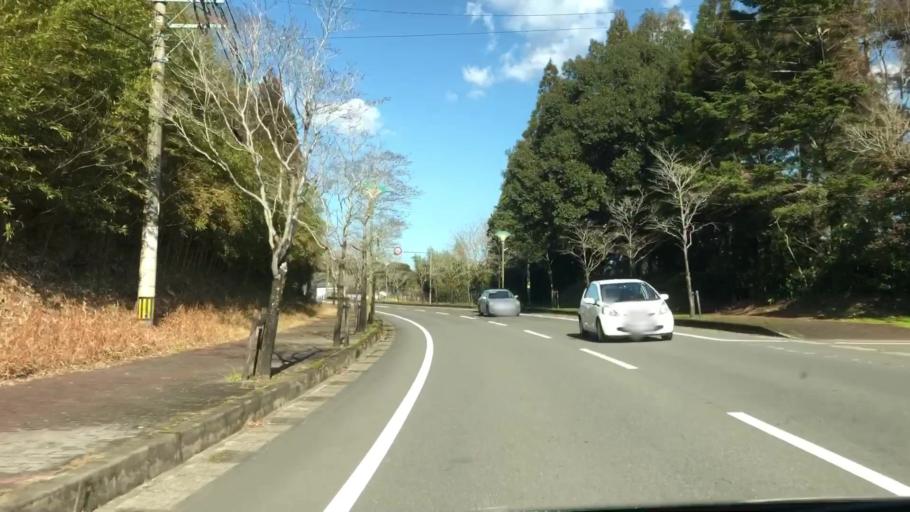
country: JP
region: Kagoshima
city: Satsumasendai
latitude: 31.8254
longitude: 130.4343
